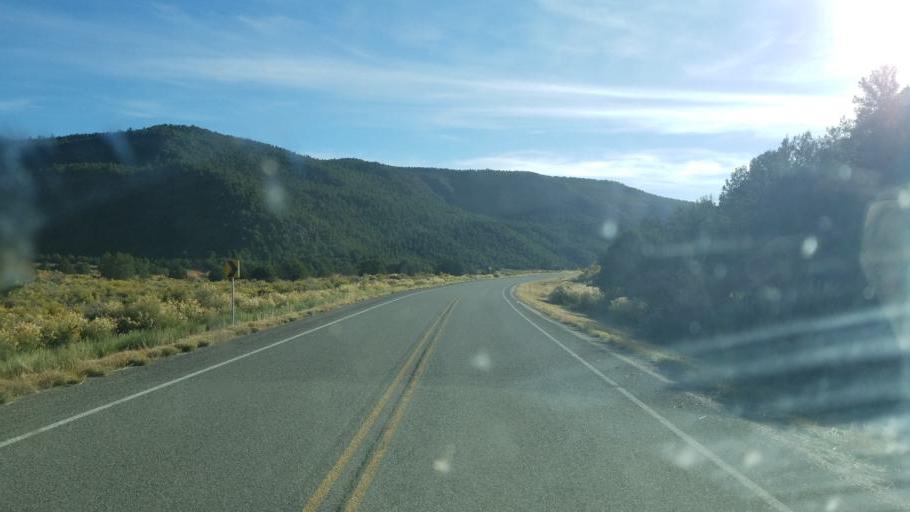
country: US
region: New Mexico
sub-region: Rio Arriba County
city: Navajo
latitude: 36.7170
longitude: -107.2844
